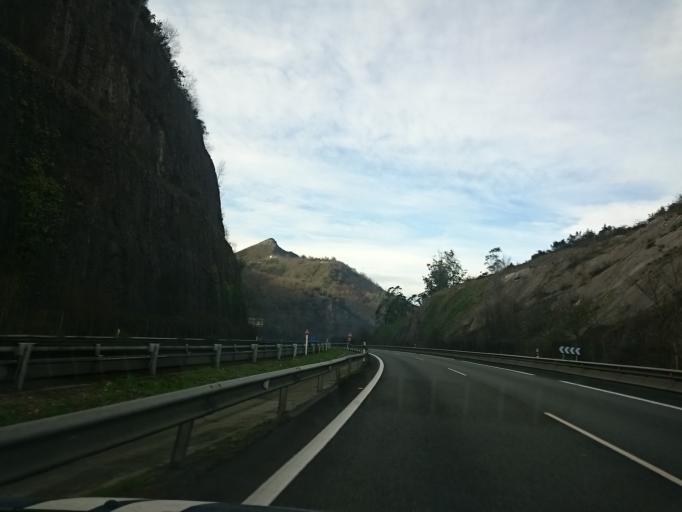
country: ES
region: Asturias
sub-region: Province of Asturias
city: Castandiello
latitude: 43.3007
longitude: -5.8492
